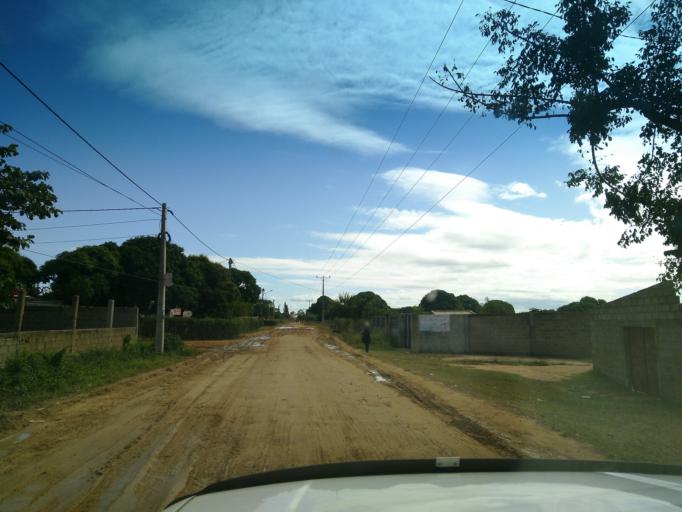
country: MZ
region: Maputo City
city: Maputo
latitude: -25.9965
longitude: 32.5388
